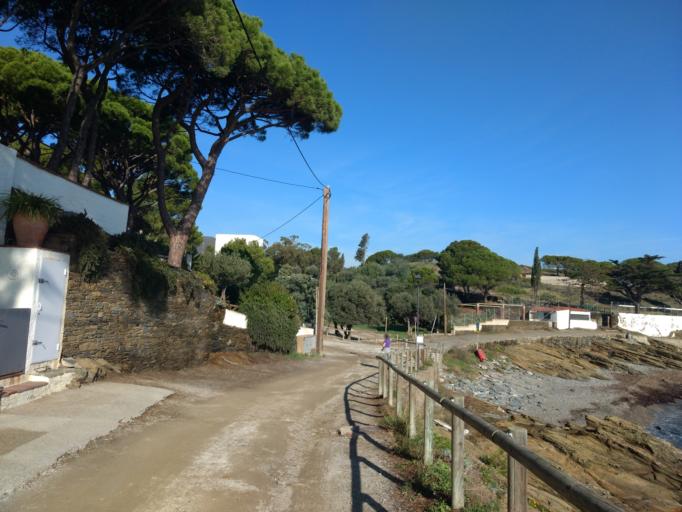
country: ES
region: Catalonia
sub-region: Provincia de Girona
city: Cadaques
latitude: 42.2803
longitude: 3.2766
